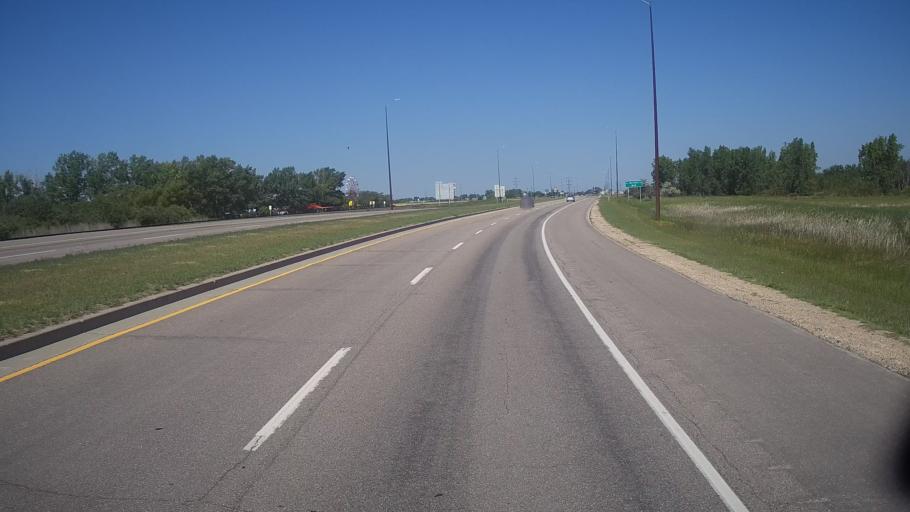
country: CA
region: Manitoba
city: Winnipeg
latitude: 49.8367
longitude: -96.9750
